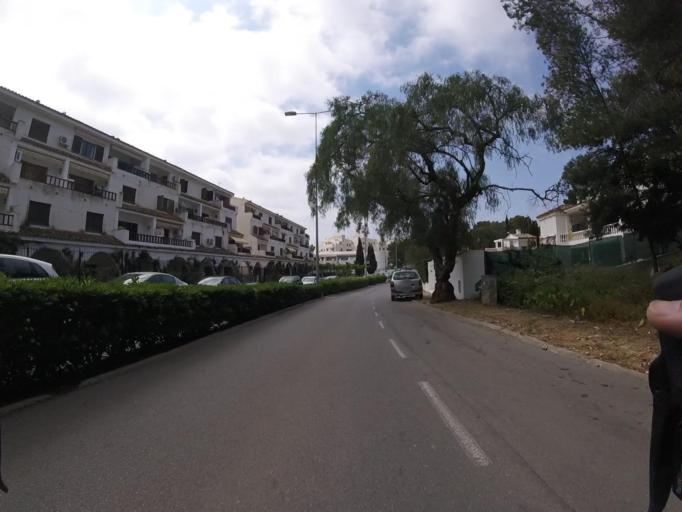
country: ES
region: Valencia
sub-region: Provincia de Castello
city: Alcoceber
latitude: 40.2530
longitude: 0.2831
